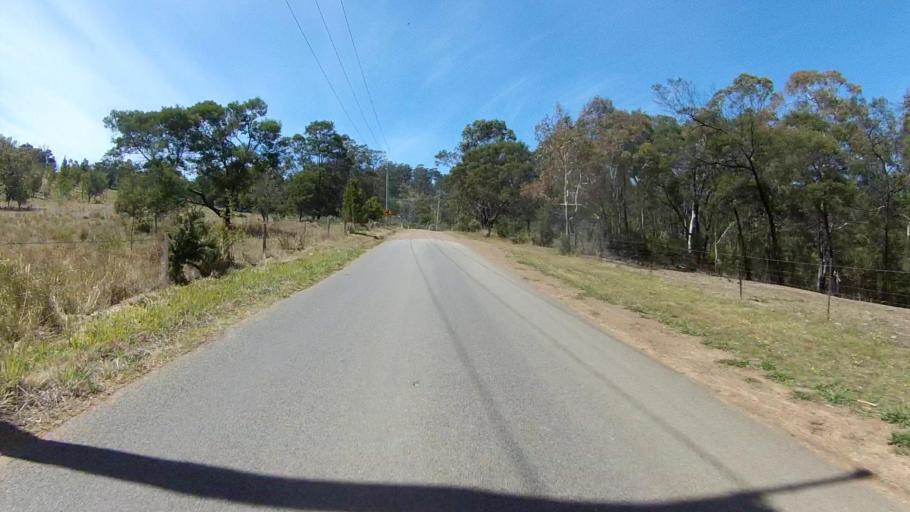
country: AU
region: Tasmania
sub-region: Sorell
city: Sorell
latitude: -42.7662
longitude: 147.6507
